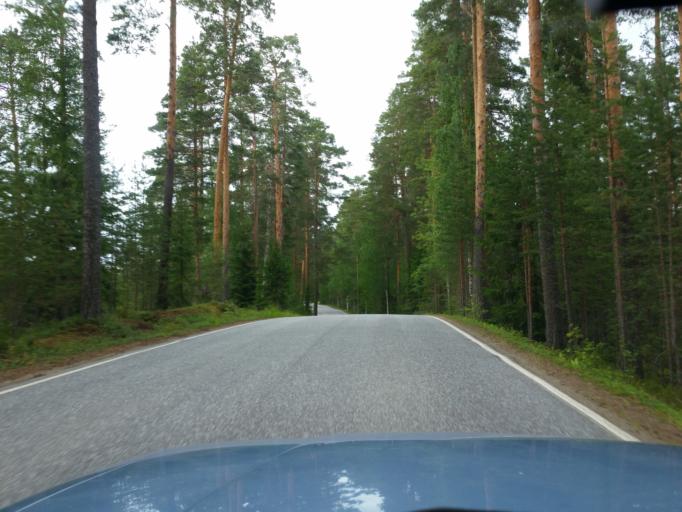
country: FI
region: Southern Savonia
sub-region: Savonlinna
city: Sulkava
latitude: 61.7833
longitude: 28.4253
